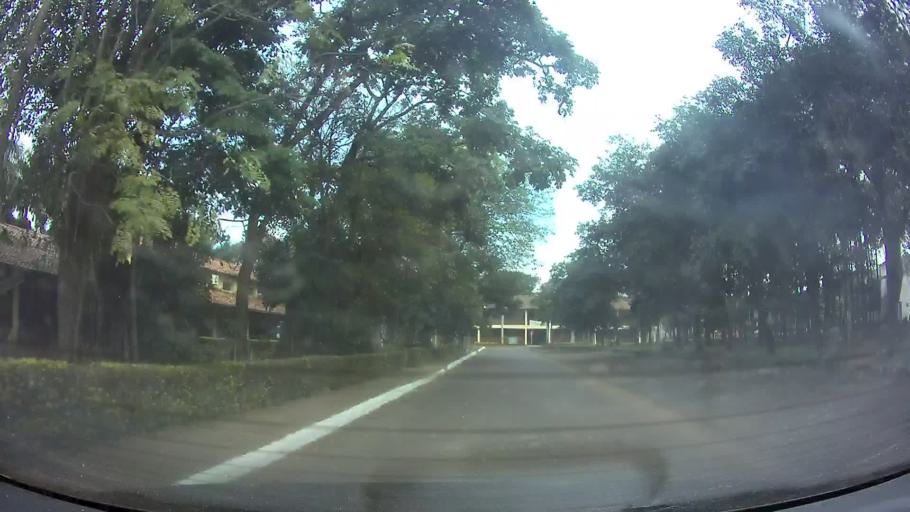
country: PY
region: Central
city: Fernando de la Mora
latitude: -25.3359
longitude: -57.5154
